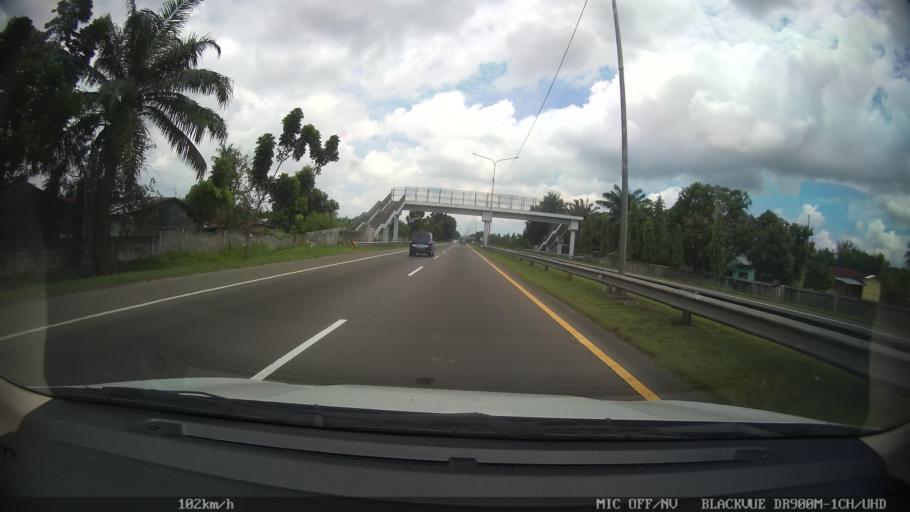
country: ID
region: North Sumatra
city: Medan
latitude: 3.6150
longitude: 98.7212
